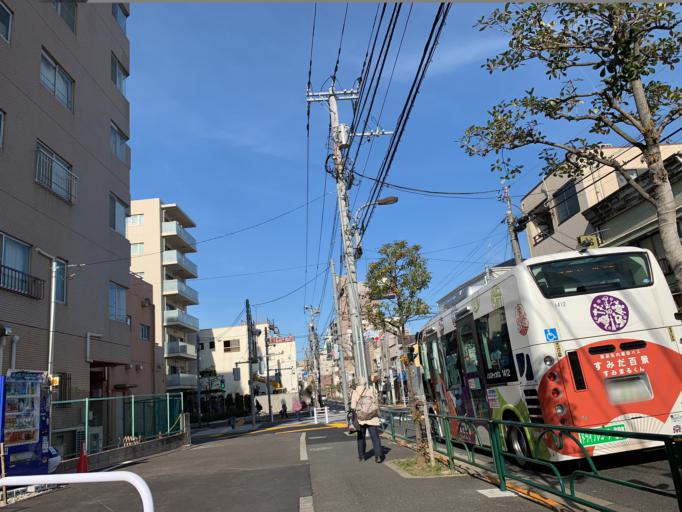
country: JP
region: Tokyo
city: Urayasu
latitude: 35.7152
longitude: 139.8199
